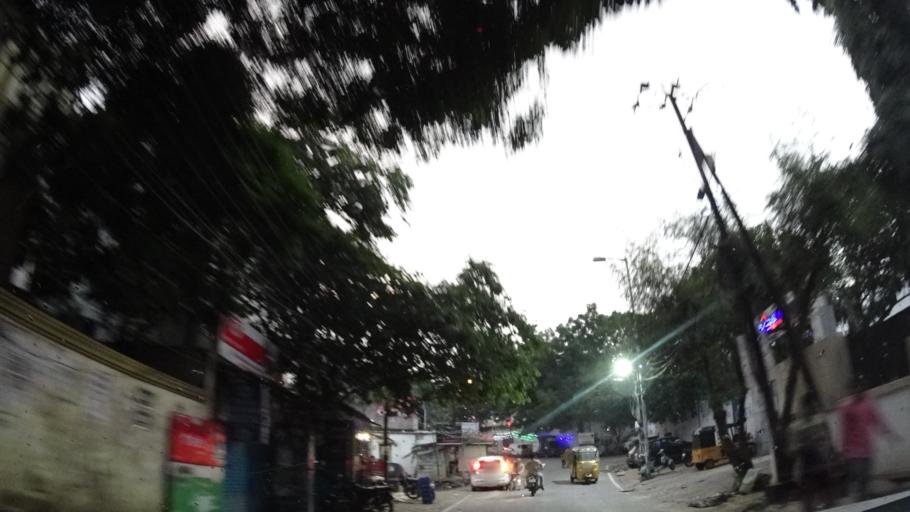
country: IN
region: Telangana
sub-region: Hyderabad
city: Hyderabad
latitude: 17.4206
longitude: 78.4436
